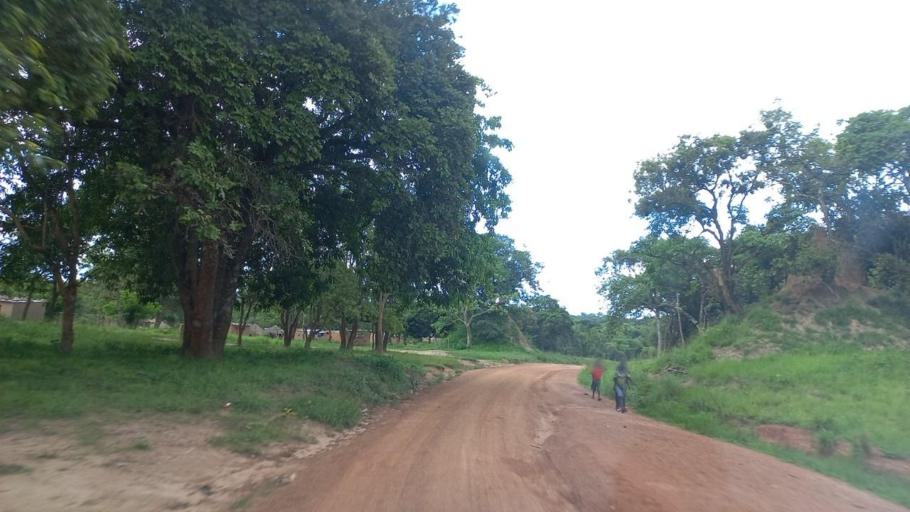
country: ZM
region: North-Western
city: Mwinilunga
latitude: -11.8406
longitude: 24.3649
